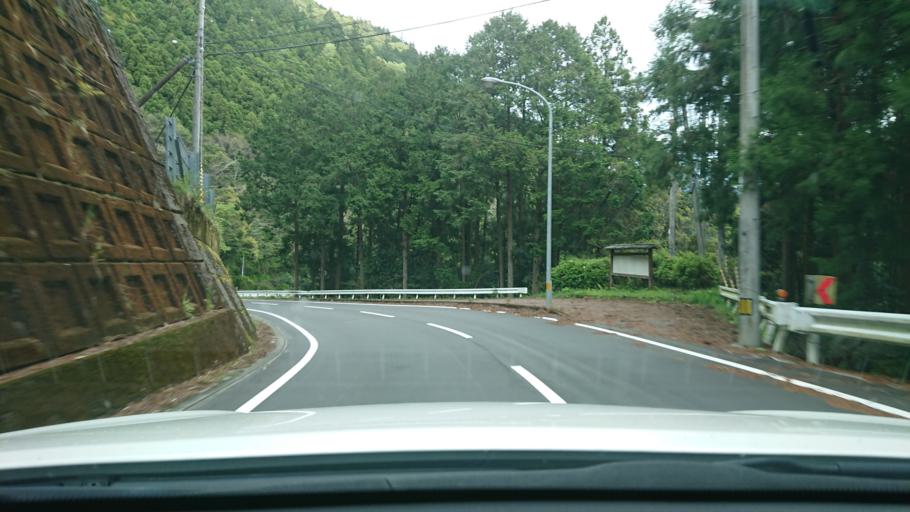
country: JP
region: Tokushima
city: Ishii
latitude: 33.9069
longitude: 134.4205
